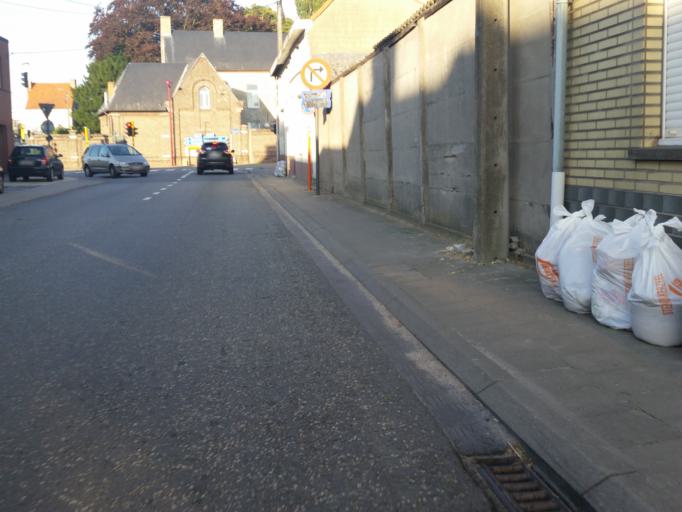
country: BE
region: Flanders
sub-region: Provincie Vlaams-Brabant
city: Steenokkerzeel
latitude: 50.9352
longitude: 4.4951
